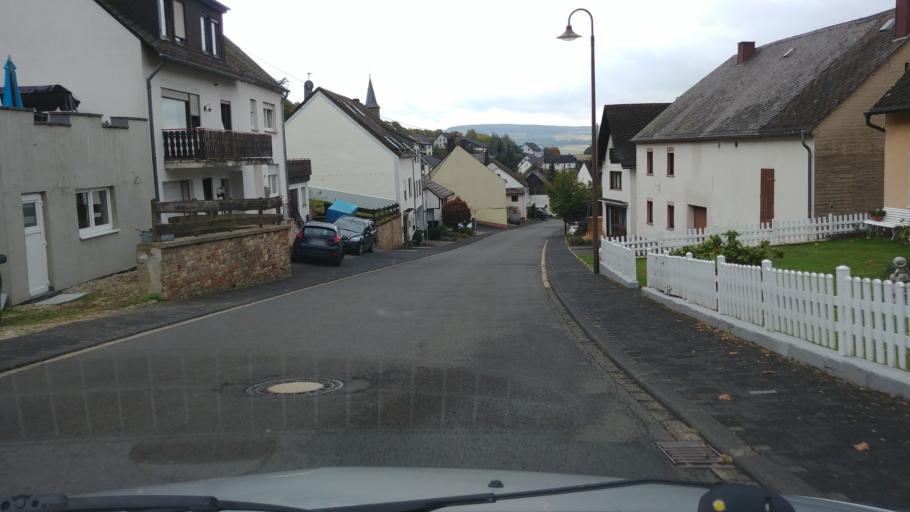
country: DE
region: Rheinland-Pfalz
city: Horath
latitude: 49.8134
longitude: 6.9867
